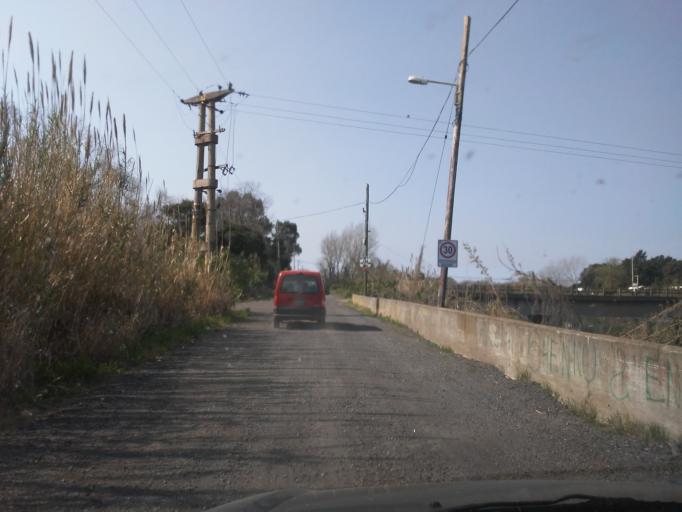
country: AR
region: Buenos Aires
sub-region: Partido de Avellaneda
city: Avellaneda
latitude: -34.6725
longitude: -58.3060
